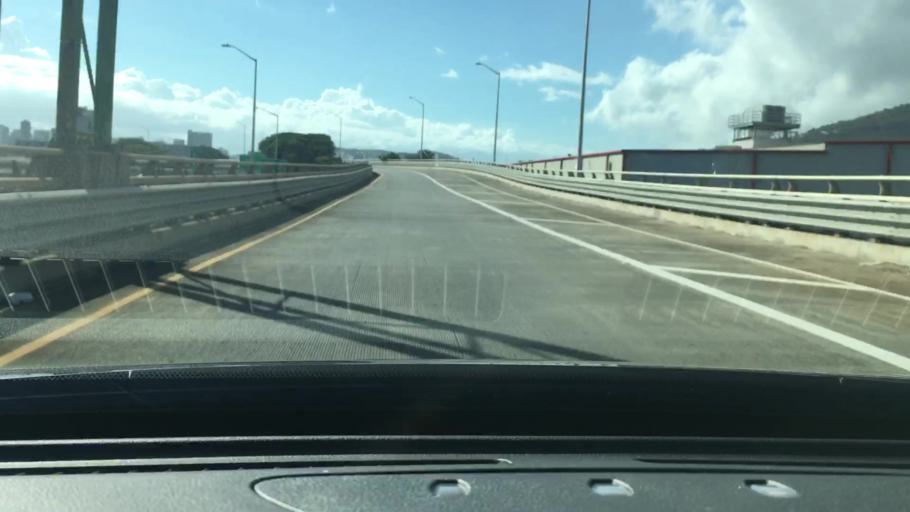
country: US
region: Hawaii
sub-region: Honolulu County
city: Honolulu
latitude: 21.2886
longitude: -157.8136
